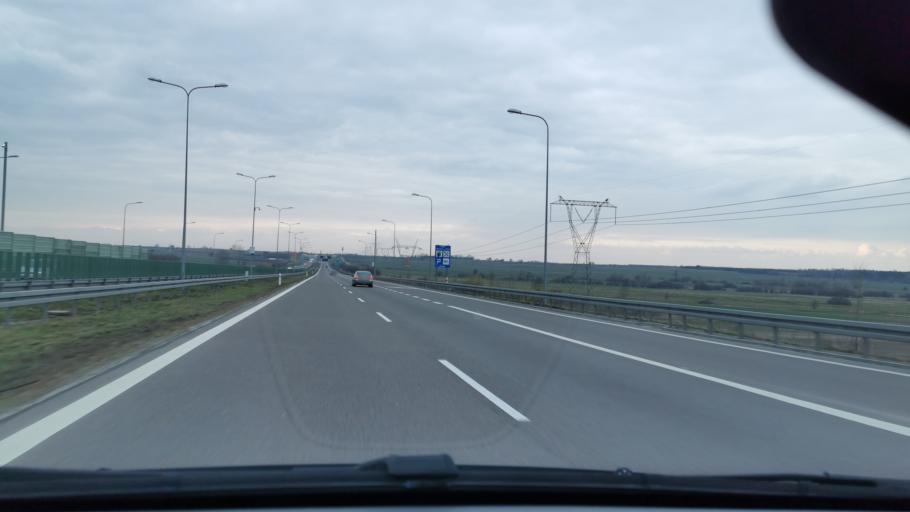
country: PL
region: Lublin Voivodeship
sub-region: Powiat pulawski
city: Markuszow
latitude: 51.3821
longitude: 22.2833
